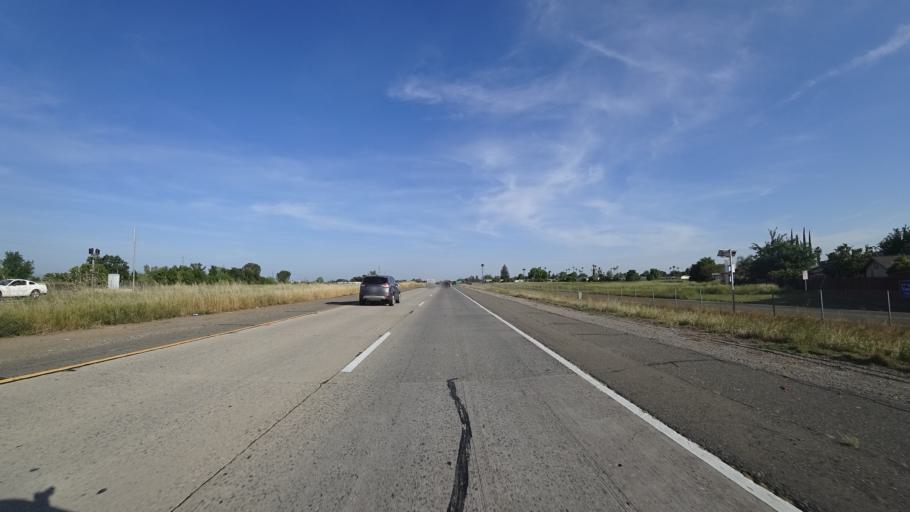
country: US
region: California
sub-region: Yuba County
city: Olivehurst
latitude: 39.0838
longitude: -121.5334
